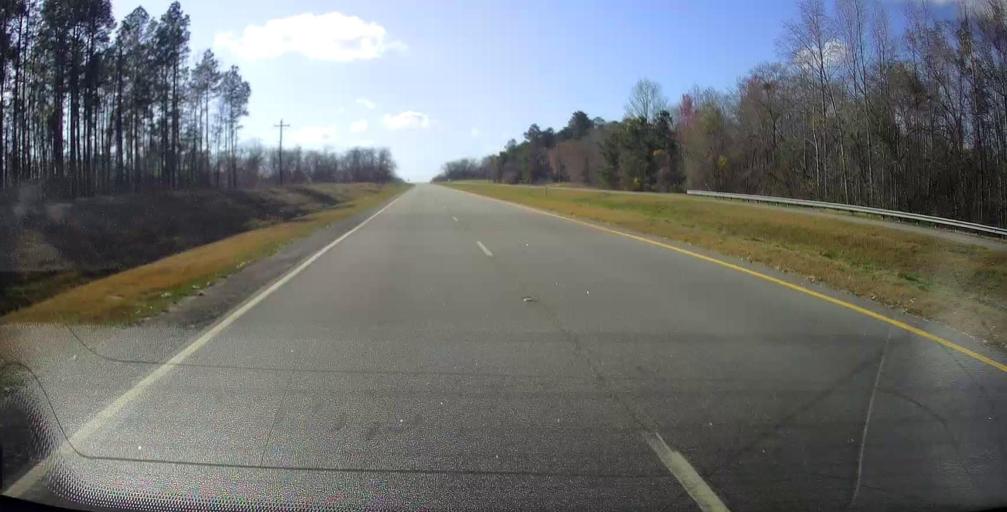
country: US
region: Georgia
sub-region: Dodge County
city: Eastman
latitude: 32.1976
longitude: -83.2173
